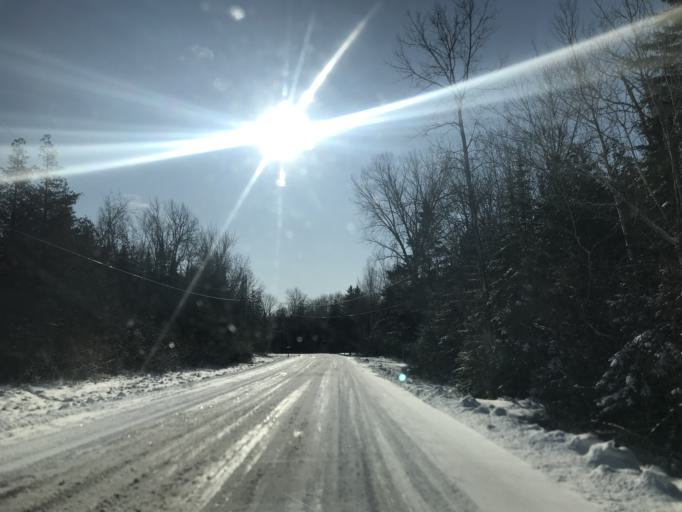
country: US
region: Wisconsin
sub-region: Door County
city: Sturgeon Bay
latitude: 44.8489
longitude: -87.5103
